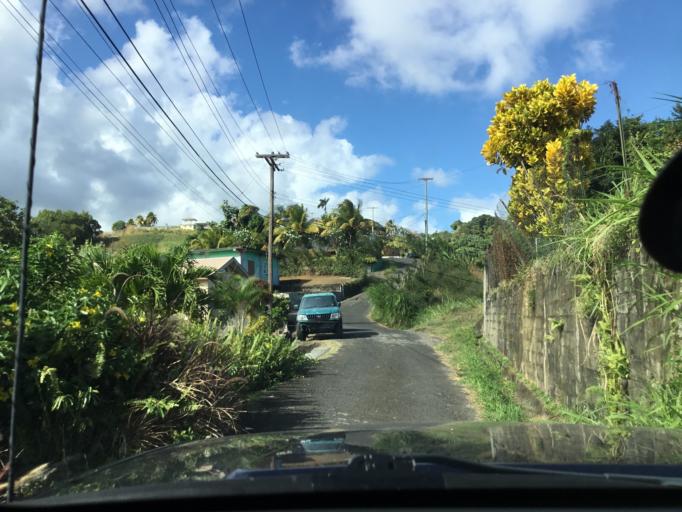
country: VC
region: Saint George
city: Kingstown
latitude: 13.1490
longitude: -61.1790
